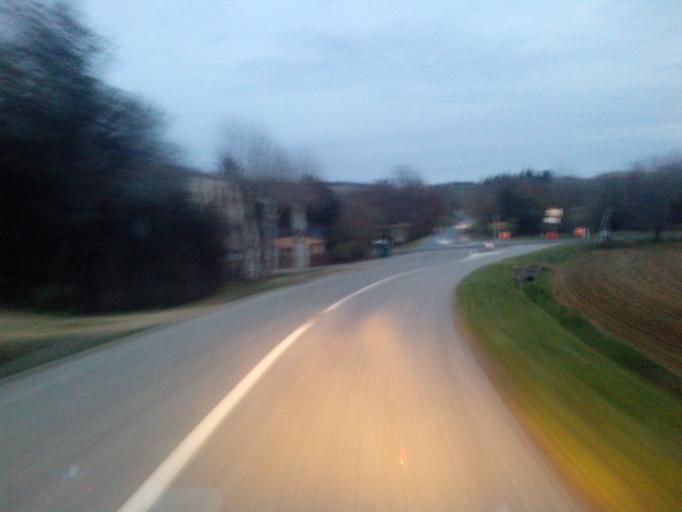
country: FR
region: Midi-Pyrenees
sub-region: Departement de la Haute-Garonne
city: Avignonet-Lauragais
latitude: 43.2802
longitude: 1.7930
